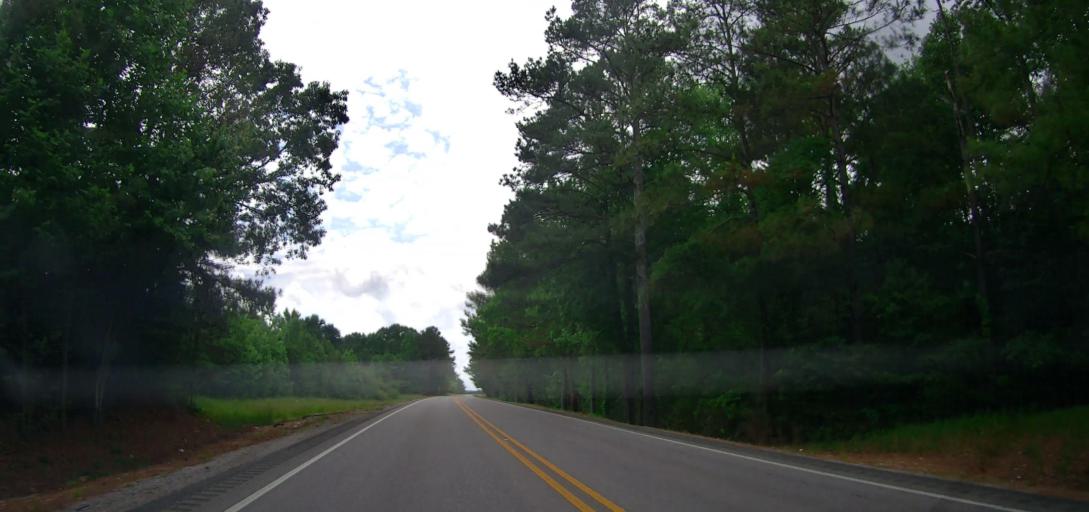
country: US
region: Alabama
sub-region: Marion County
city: Hamilton
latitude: 34.1255
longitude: -88.0345
